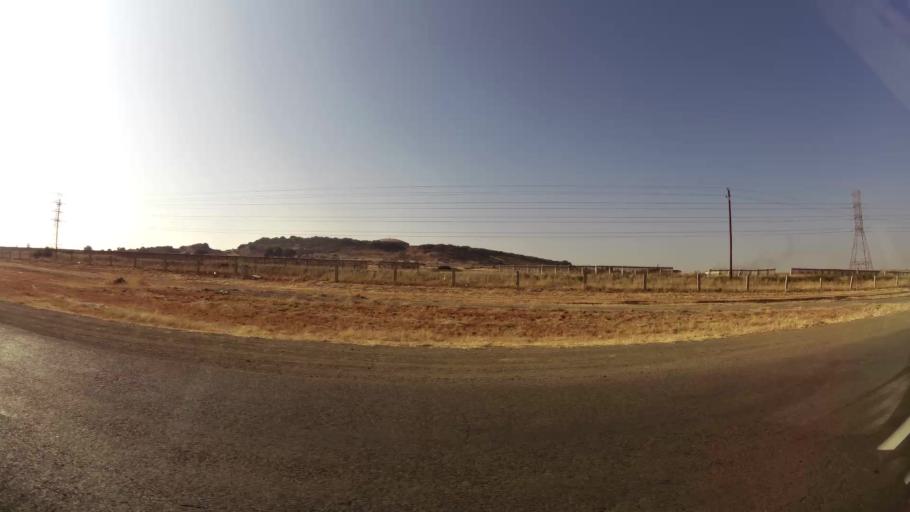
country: ZA
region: Orange Free State
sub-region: Mangaung Metropolitan Municipality
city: Bloemfontein
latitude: -29.1754
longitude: 26.1927
